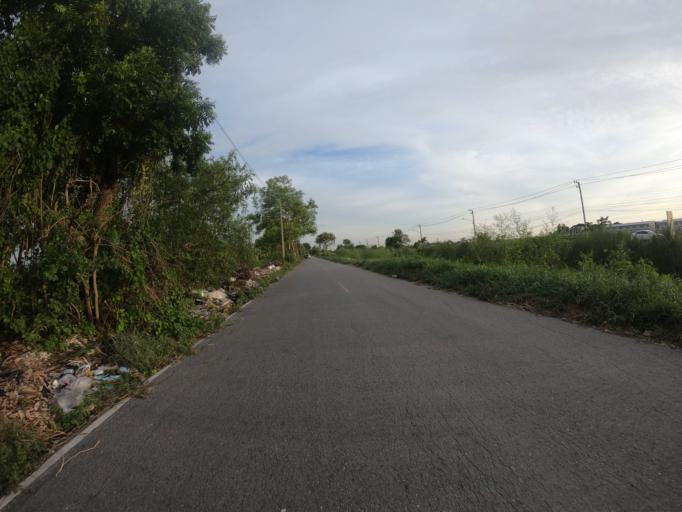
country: TH
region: Pathum Thani
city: Ban Rangsit
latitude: 14.0406
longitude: 100.8013
